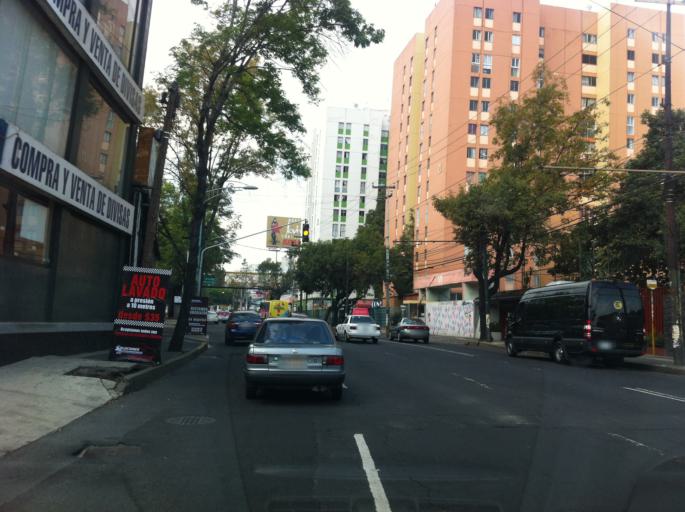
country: MX
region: Mexico City
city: Coyoacan
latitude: 19.3377
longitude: -99.1849
